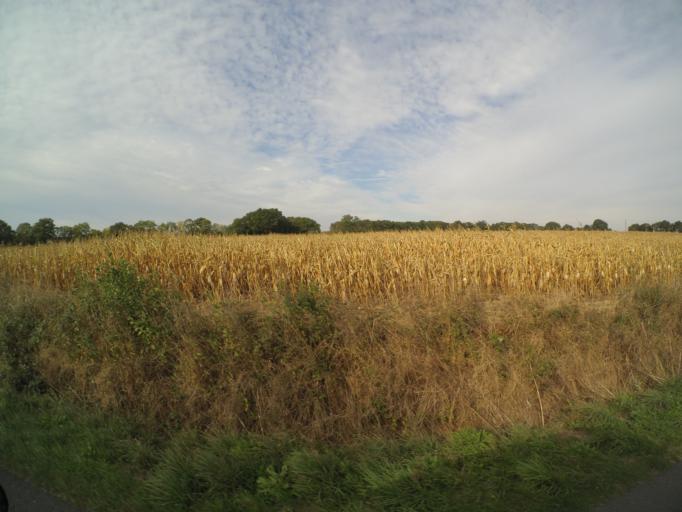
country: FR
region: Pays de la Loire
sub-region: Departement de Maine-et-Loire
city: Villedieu-la-Blouere
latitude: 47.1699
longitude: -1.0474
